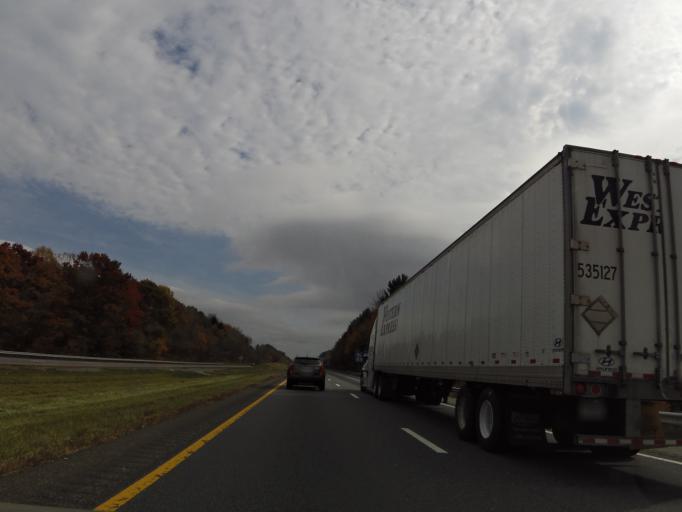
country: US
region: Virginia
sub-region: Carroll County
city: Hillsville
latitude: 36.6923
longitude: -80.7312
